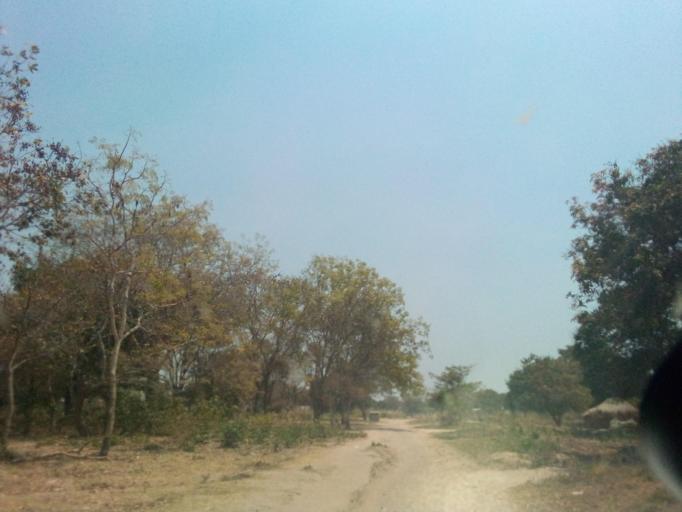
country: ZM
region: Copperbelt
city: Kataba
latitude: -12.2379
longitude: 30.3130
